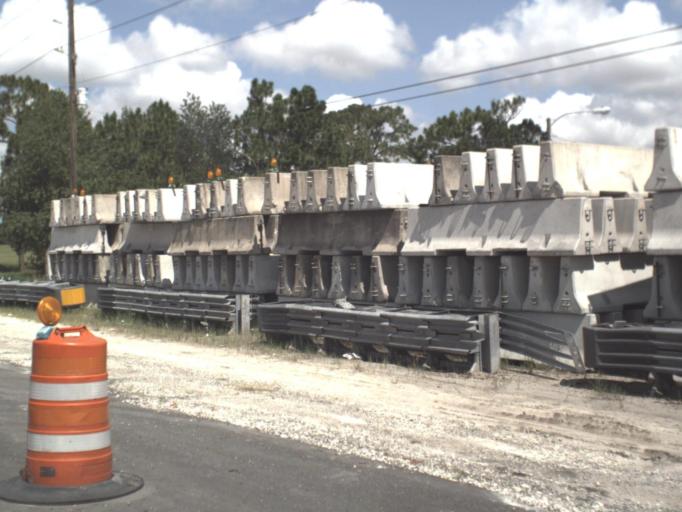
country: US
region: Florida
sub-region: Hernando County
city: Brookridge
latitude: 28.5340
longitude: -82.4845
